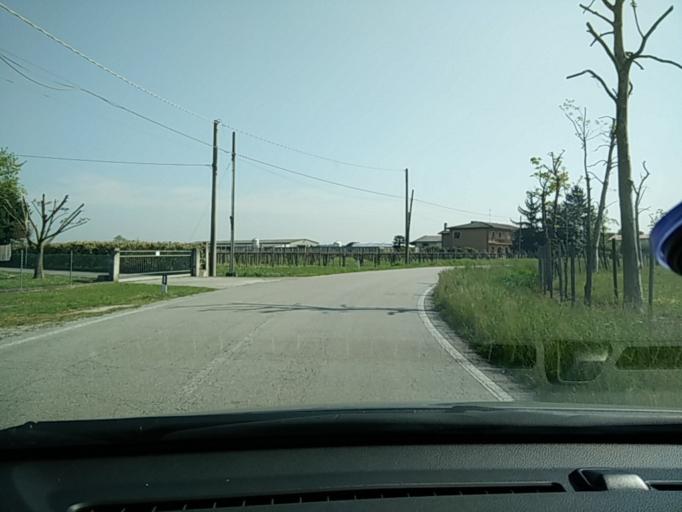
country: IT
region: Veneto
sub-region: Provincia di Treviso
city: Fornaci
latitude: 45.6688
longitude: 12.4462
